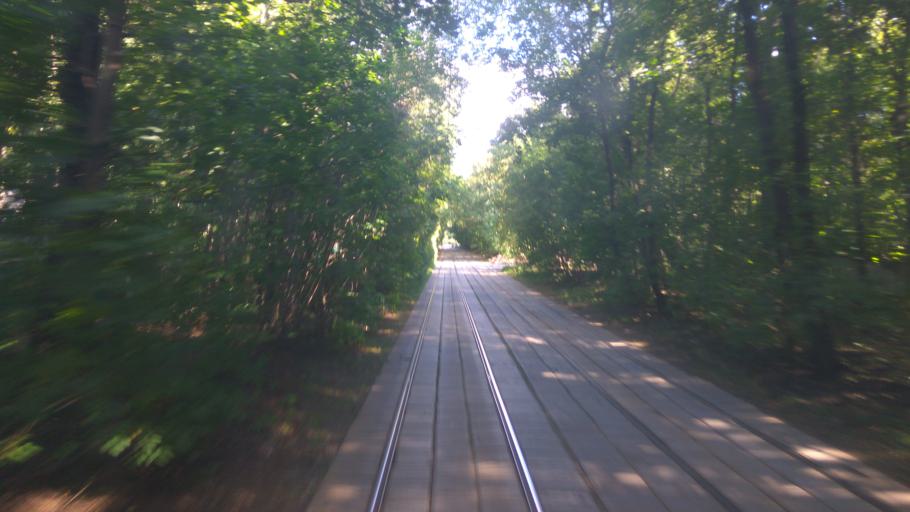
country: RU
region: Moscow
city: Sokol'niki
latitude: 55.8078
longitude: 37.6888
